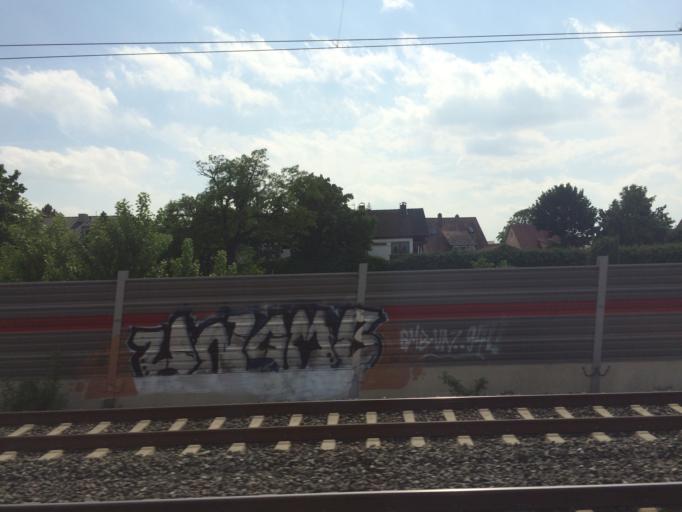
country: DE
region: Bavaria
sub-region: Regierungsbezirk Mittelfranken
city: Wetzendorf
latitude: 49.4547
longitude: 11.0313
